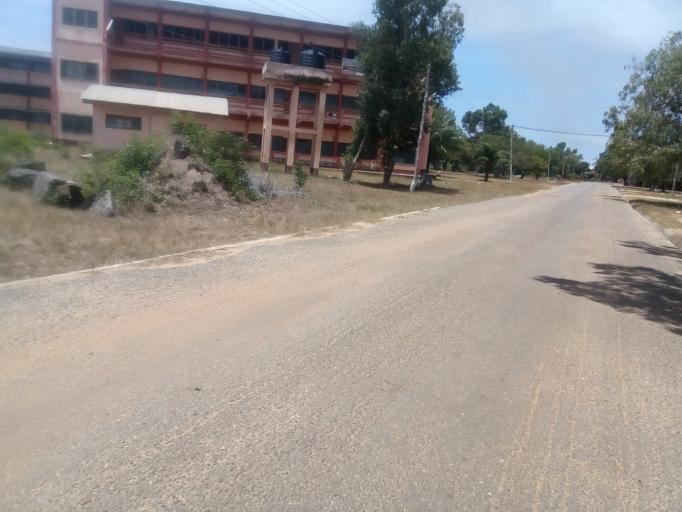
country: GH
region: Volta
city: Anloga
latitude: 5.8023
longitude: 0.6152
